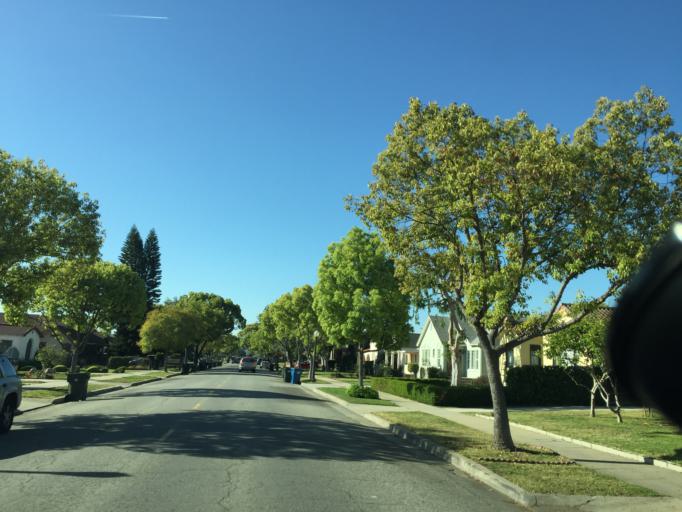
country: US
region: California
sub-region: Los Angeles County
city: Alhambra
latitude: 34.0824
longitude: -118.1198
